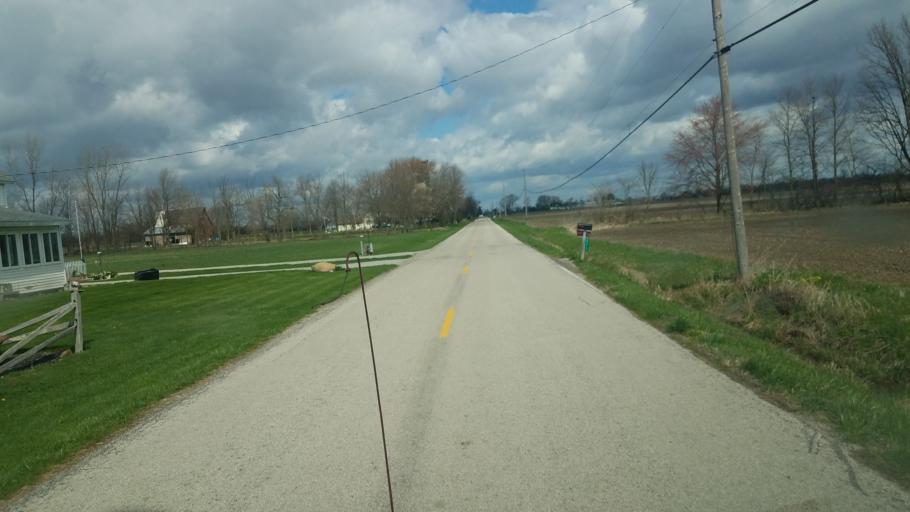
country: US
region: Ohio
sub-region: Union County
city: Richwood
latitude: 40.4050
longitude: -83.3079
